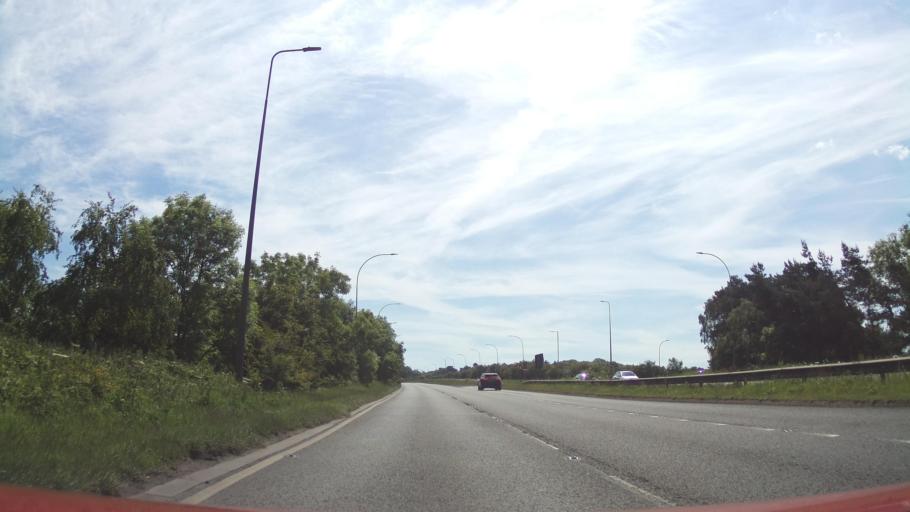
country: GB
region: England
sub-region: North Lincolnshire
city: Broughton
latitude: 53.5559
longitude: -0.5861
